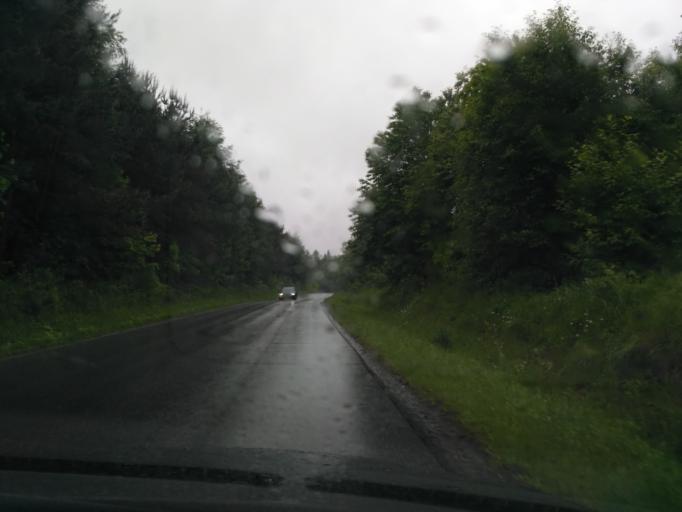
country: PL
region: Subcarpathian Voivodeship
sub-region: Powiat jasielski
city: Debowiec
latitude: 49.6642
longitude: 21.4434
